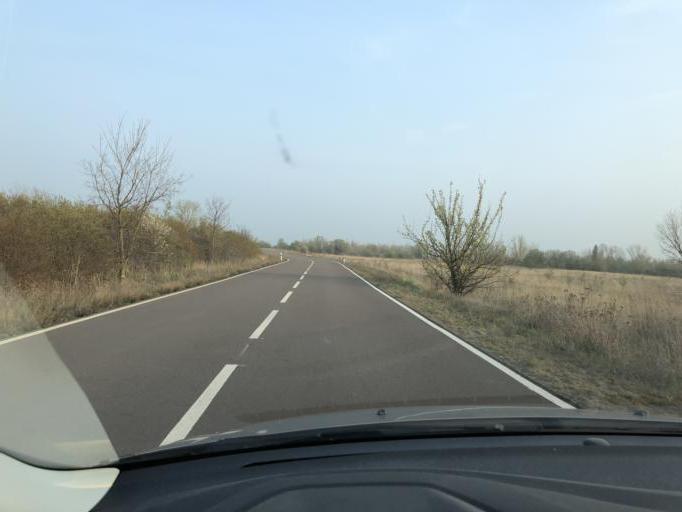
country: DE
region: Saxony
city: Dobernitz
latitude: 51.5017
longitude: 12.3138
